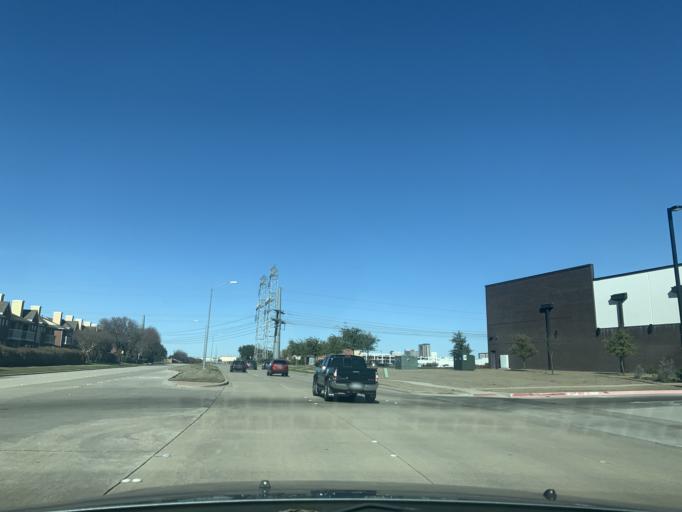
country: US
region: Texas
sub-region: Denton County
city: The Colony
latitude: 33.0570
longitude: -96.8328
